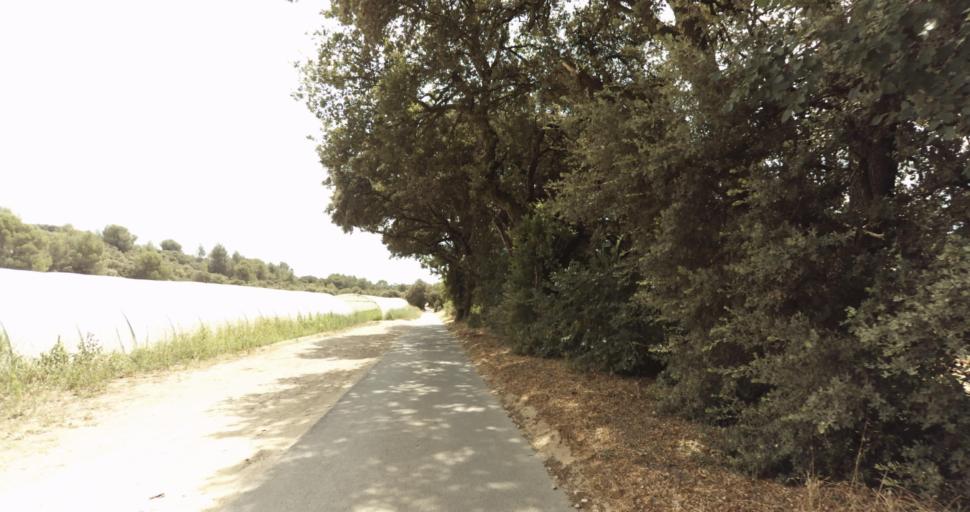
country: FR
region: Provence-Alpes-Cote d'Azur
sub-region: Departement du Vaucluse
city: Loriol-du-Comtat
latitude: 44.0610
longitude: 4.9924
